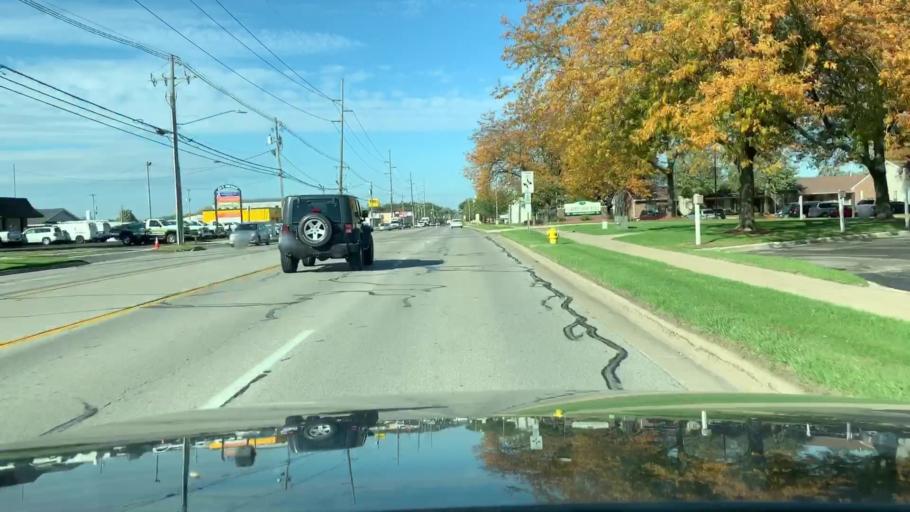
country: US
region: Michigan
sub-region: Ottawa County
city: Holland
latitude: 42.7932
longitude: -86.0776
